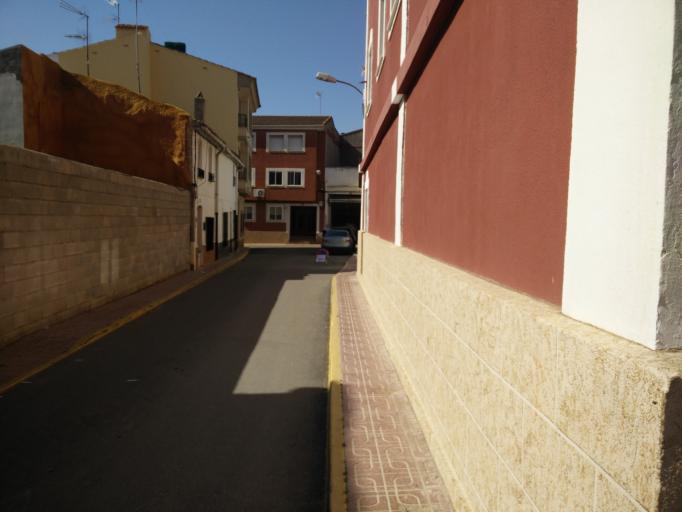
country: ES
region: Castille-La Mancha
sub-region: Provincia de Cuenca
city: Motilla del Palancar
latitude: 39.5604
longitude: -1.9103
